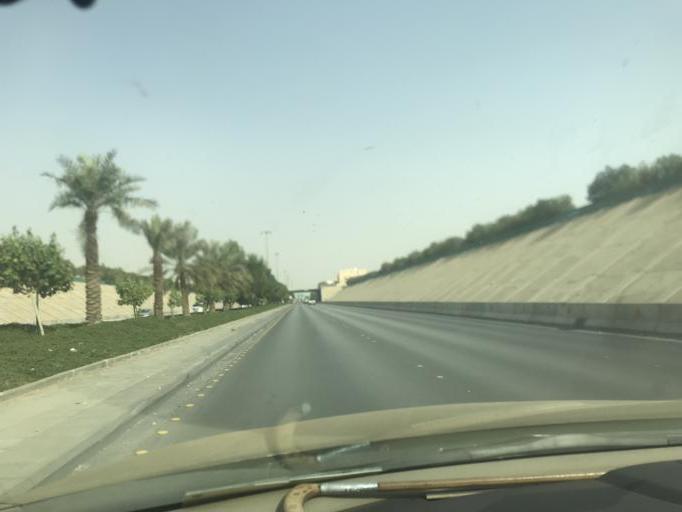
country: SA
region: Ar Riyad
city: Riyadh
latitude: 24.6673
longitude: 46.7936
